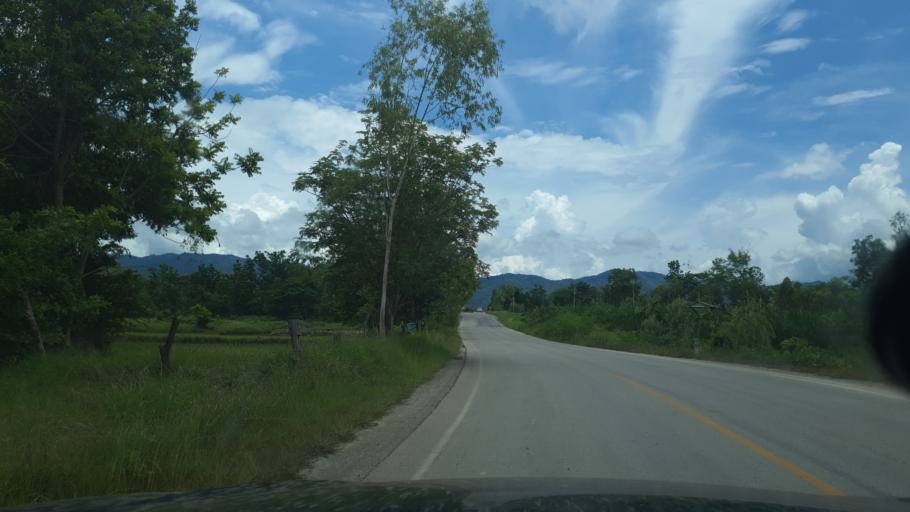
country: TH
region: Lampang
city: Sop Prap
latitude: 17.9154
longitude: 99.3883
